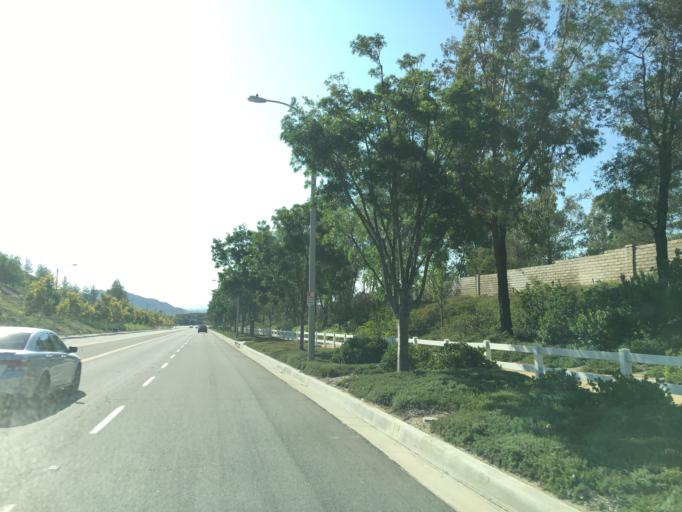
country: US
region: California
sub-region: Los Angeles County
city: Valencia
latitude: 34.4524
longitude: -118.6301
